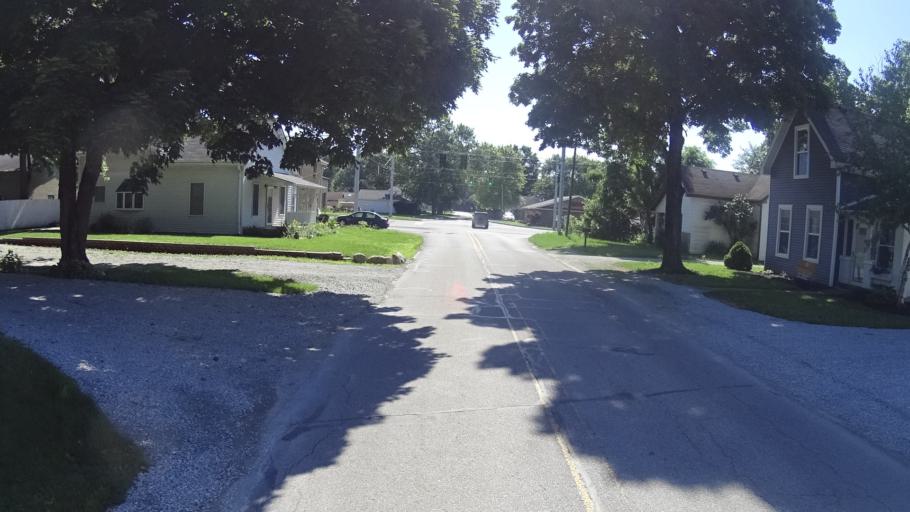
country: US
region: Indiana
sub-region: Madison County
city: Pendleton
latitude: 40.0087
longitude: -85.7308
